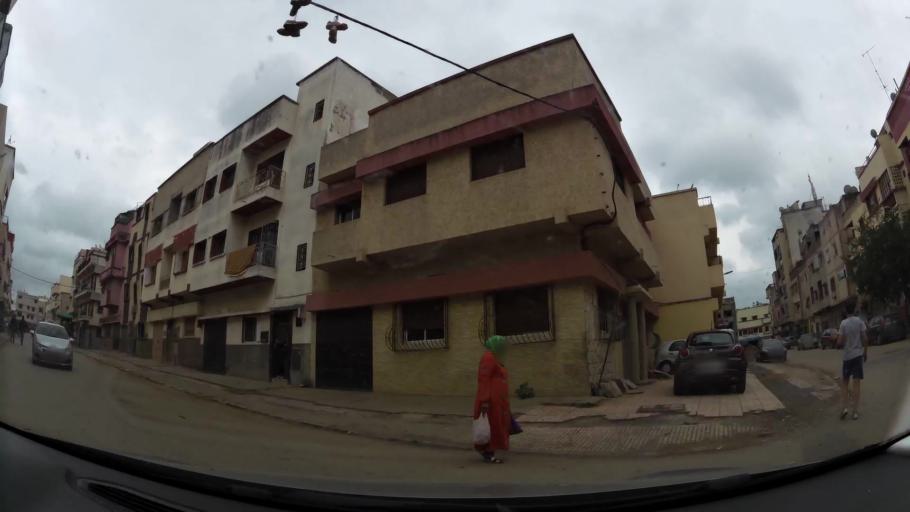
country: MA
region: Rabat-Sale-Zemmour-Zaer
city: Sale
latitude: 34.0373
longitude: -6.8056
